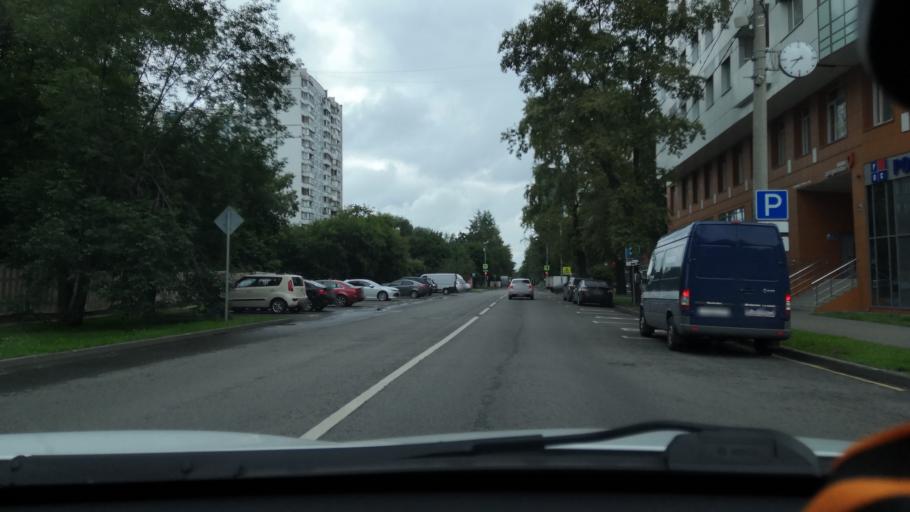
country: RU
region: Moscow
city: Vatutino
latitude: 55.8709
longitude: 37.6823
